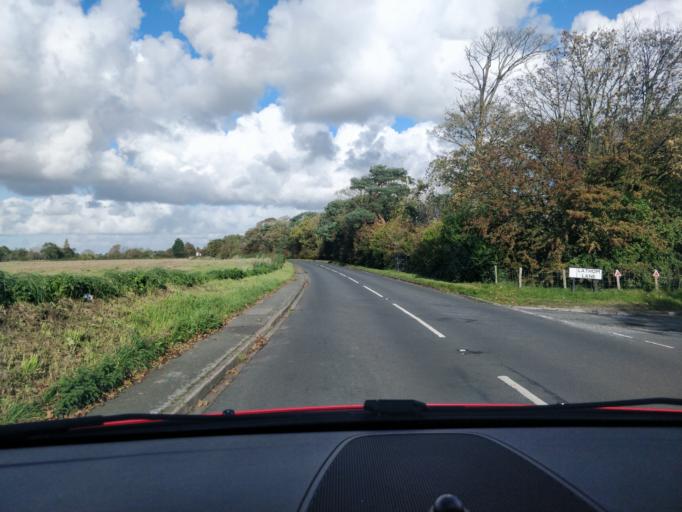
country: GB
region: England
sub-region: Lancashire
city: Ormskirk
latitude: 53.5748
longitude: -2.8591
